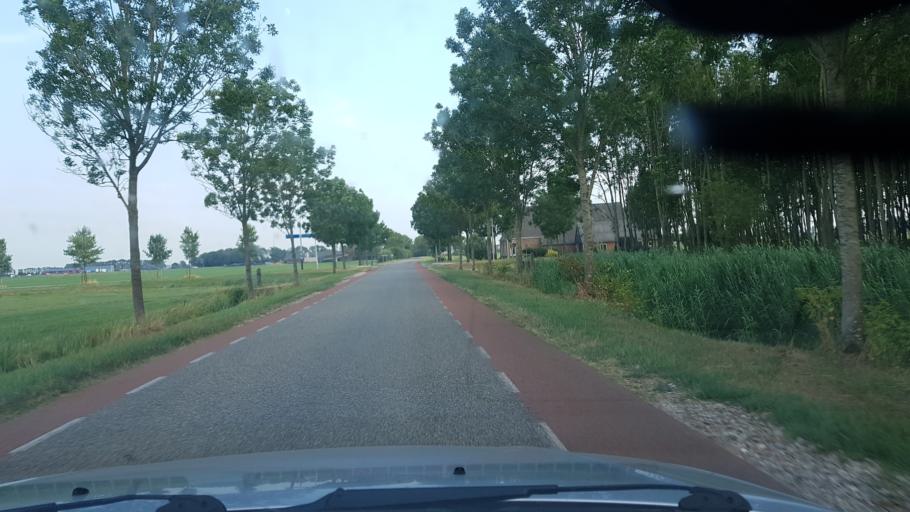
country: NL
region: Friesland
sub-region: Gemeente Ferwerderadiel
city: Burdaard
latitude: 53.3049
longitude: 5.8729
